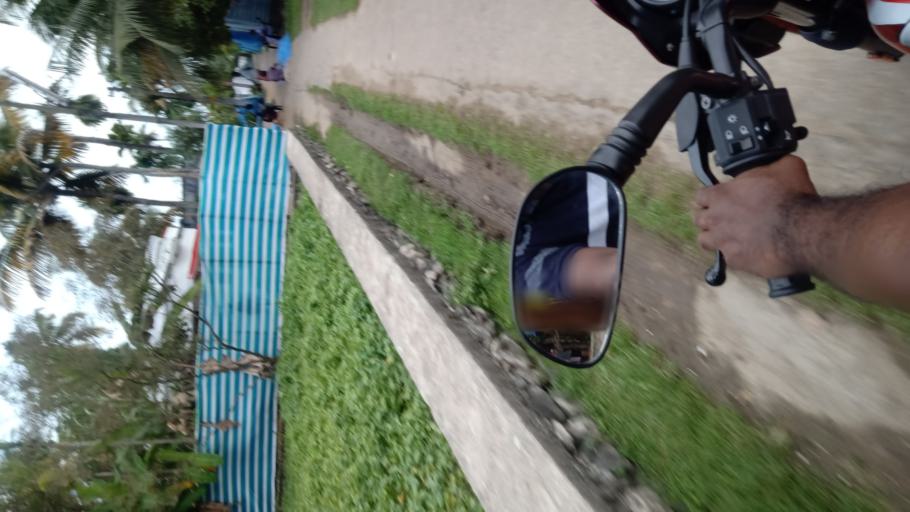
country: IN
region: Kerala
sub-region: Ernakulam
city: Elur
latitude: 10.0344
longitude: 76.2094
